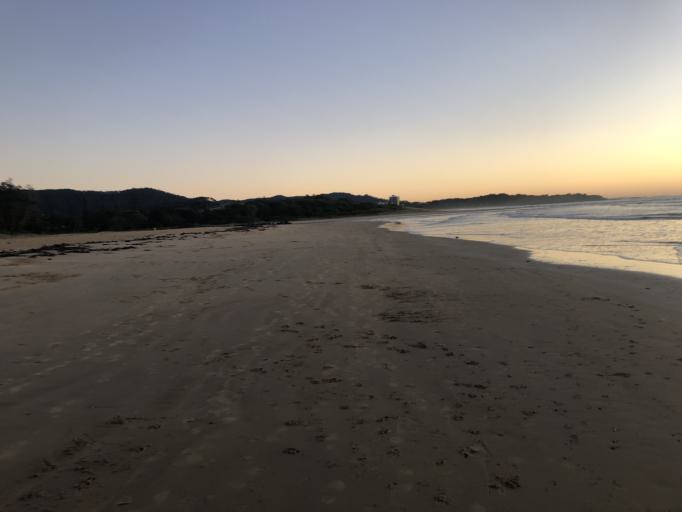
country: AU
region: New South Wales
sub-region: Coffs Harbour
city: Coffs Harbour
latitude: -30.2986
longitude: 153.1399
